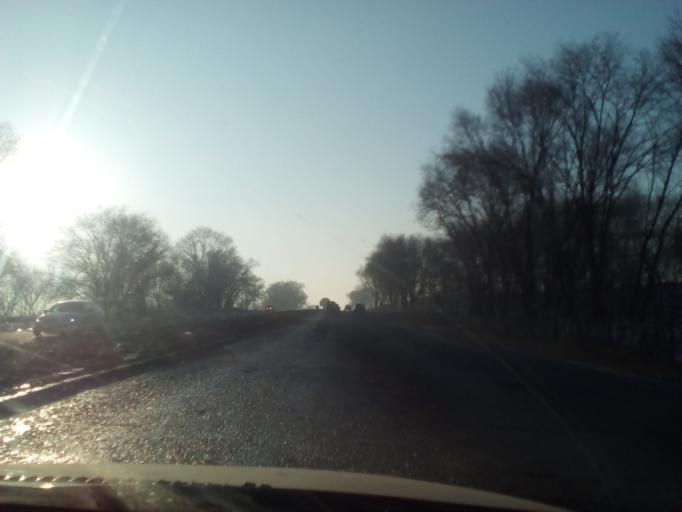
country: KZ
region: Almaty Oblysy
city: Burunday
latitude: 43.2227
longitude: 76.5792
